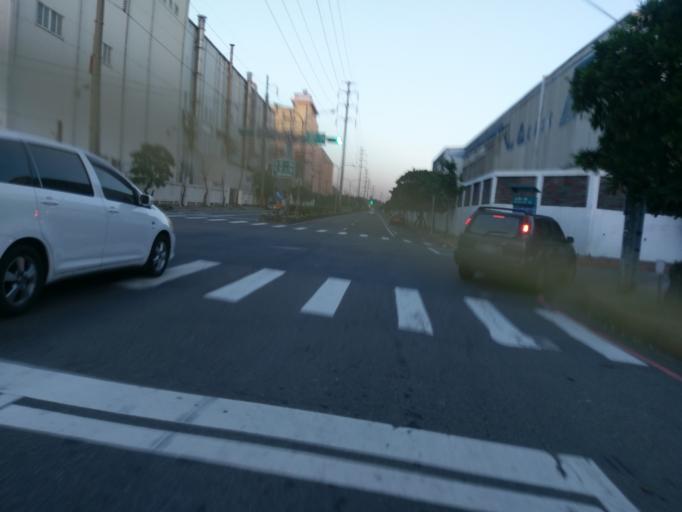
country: TW
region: Taiwan
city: Taoyuan City
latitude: 25.0551
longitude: 121.1268
